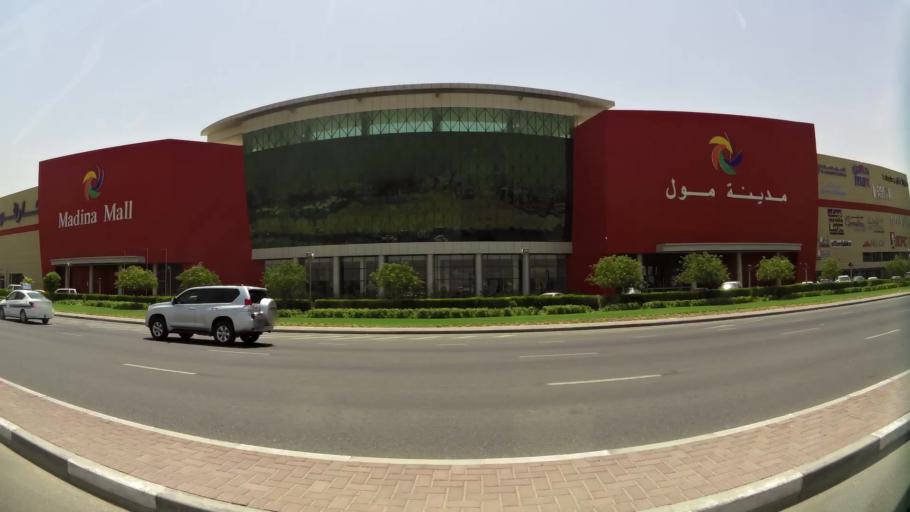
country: AE
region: Ash Shariqah
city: Sharjah
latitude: 25.2822
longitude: 55.3972
